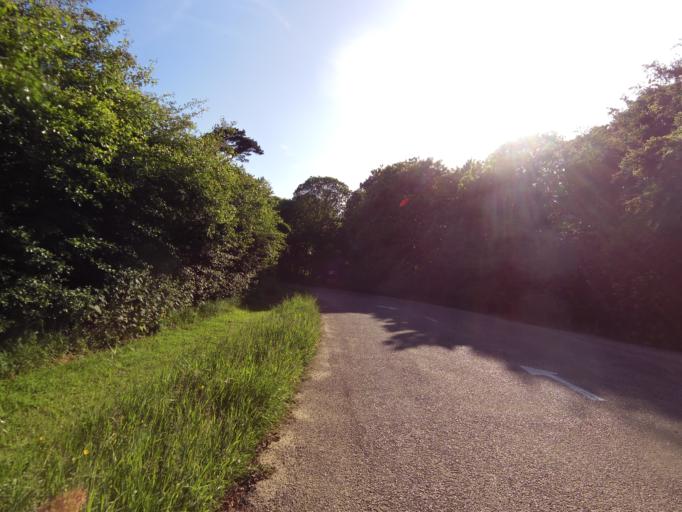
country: GB
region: England
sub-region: Suffolk
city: Woodbridge
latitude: 52.0958
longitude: 1.3432
